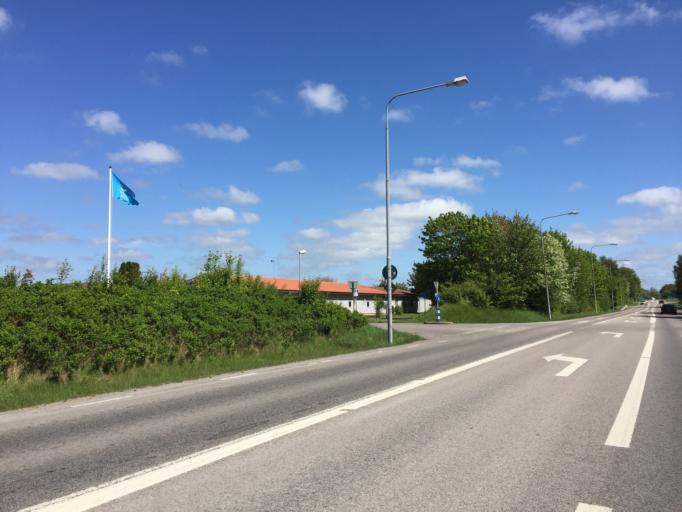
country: SE
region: Halland
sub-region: Varbergs Kommun
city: Varberg
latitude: 57.1113
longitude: 12.2833
